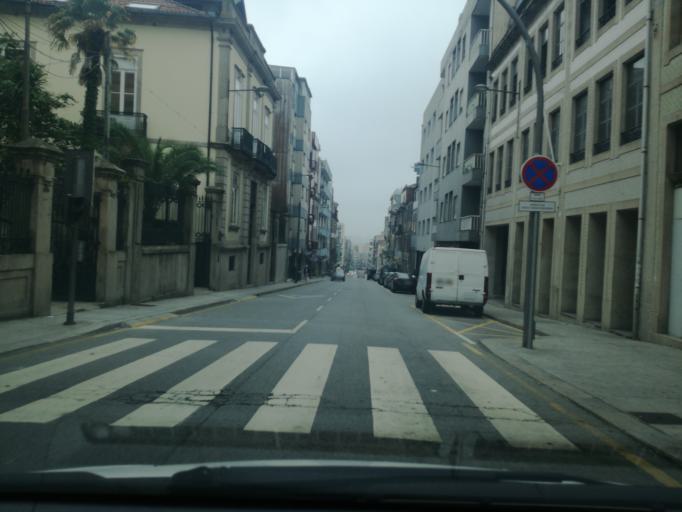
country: PT
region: Porto
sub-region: Porto
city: Porto
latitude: 41.1580
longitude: -8.6046
